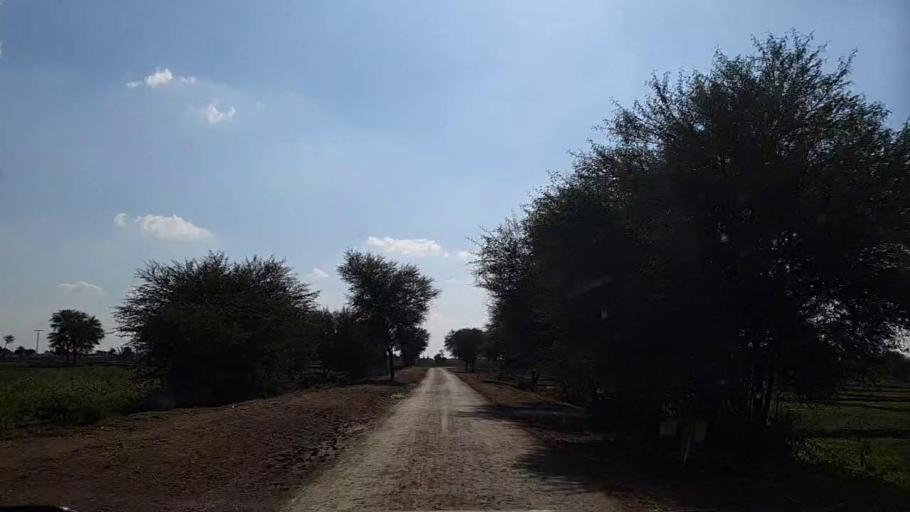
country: PK
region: Sindh
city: Pithoro
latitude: 25.6500
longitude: 69.4485
